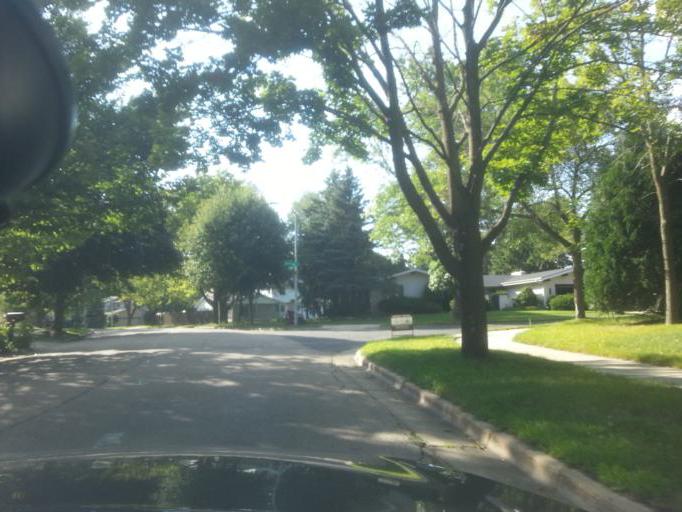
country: US
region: Wisconsin
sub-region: Dane County
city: Middleton
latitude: 43.0724
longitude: -89.4966
